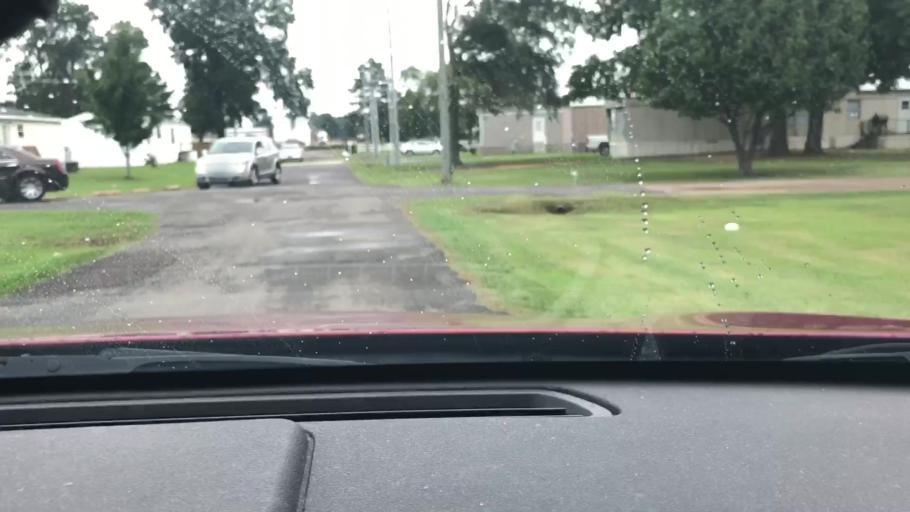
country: US
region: Texas
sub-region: Bowie County
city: Nash
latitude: 33.4434
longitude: -94.1381
